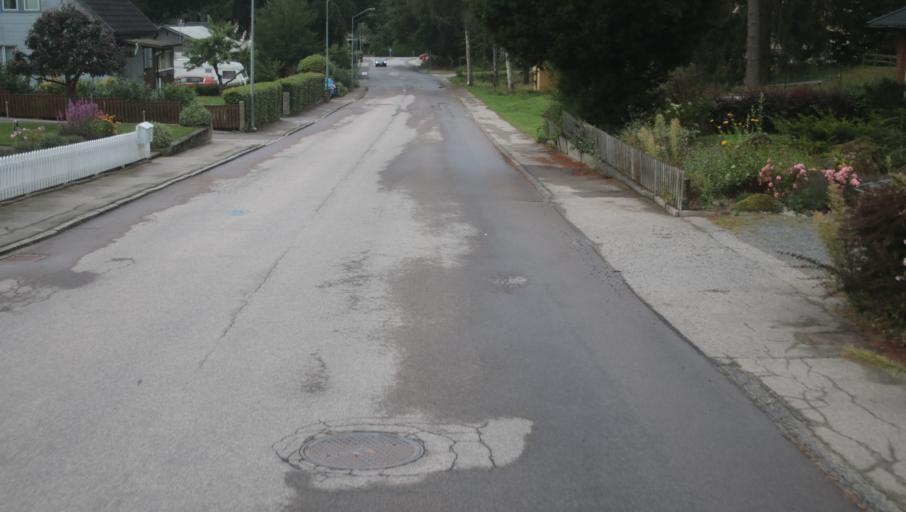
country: SE
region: Blekinge
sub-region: Karlshamns Kommun
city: Svangsta
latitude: 56.2592
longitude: 14.7787
